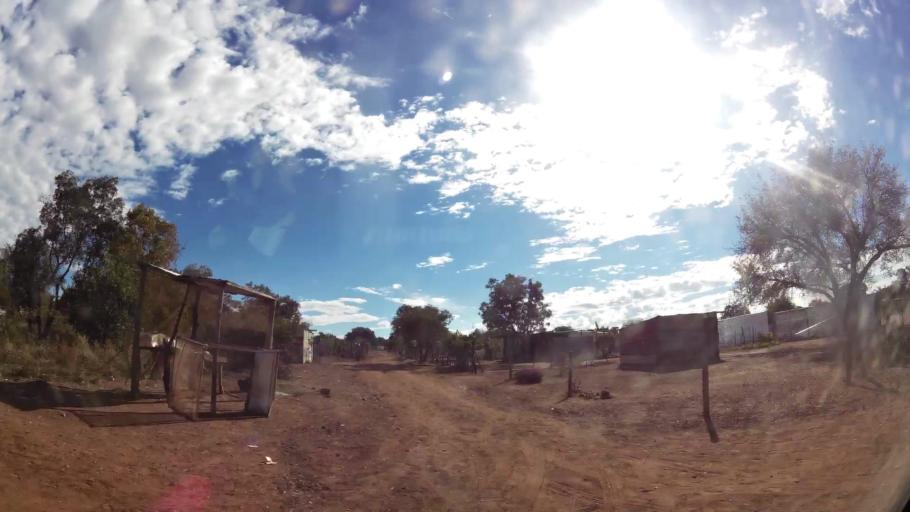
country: ZA
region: Limpopo
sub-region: Waterberg District Municipality
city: Warmbaths
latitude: -24.8754
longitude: 28.2764
